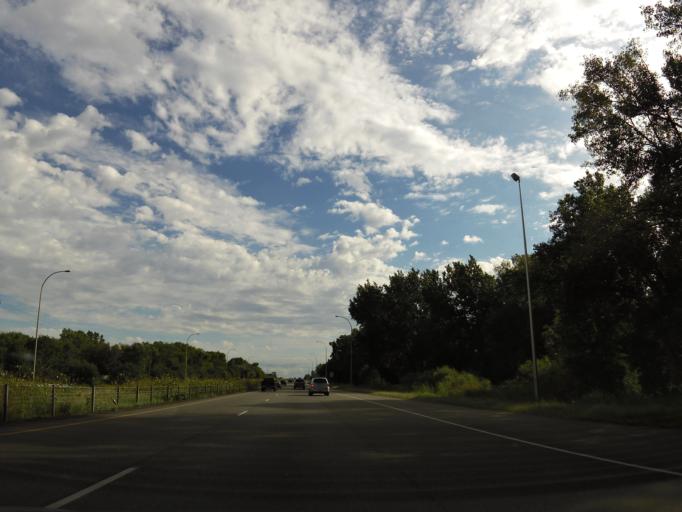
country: US
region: Minnesota
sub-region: Hennepin County
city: Osseo
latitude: 45.0789
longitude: -93.4022
